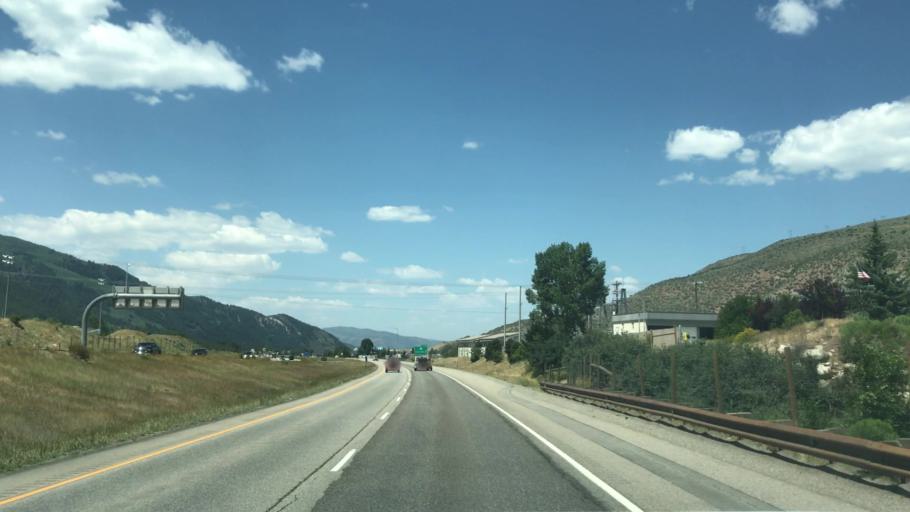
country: US
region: Colorado
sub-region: Eagle County
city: Minturn
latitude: 39.6201
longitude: -106.4703
